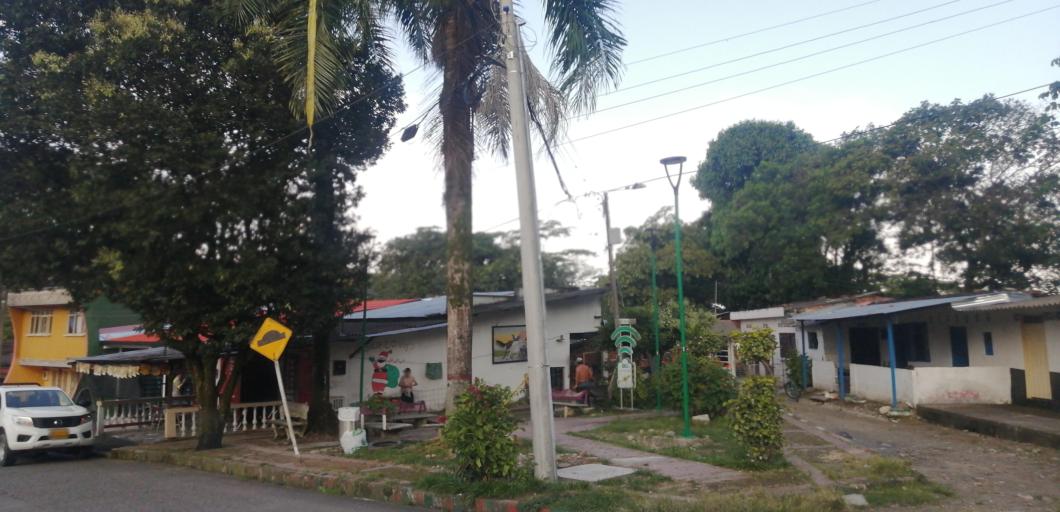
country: CO
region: Meta
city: Acacias
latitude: 3.9828
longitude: -73.7586
